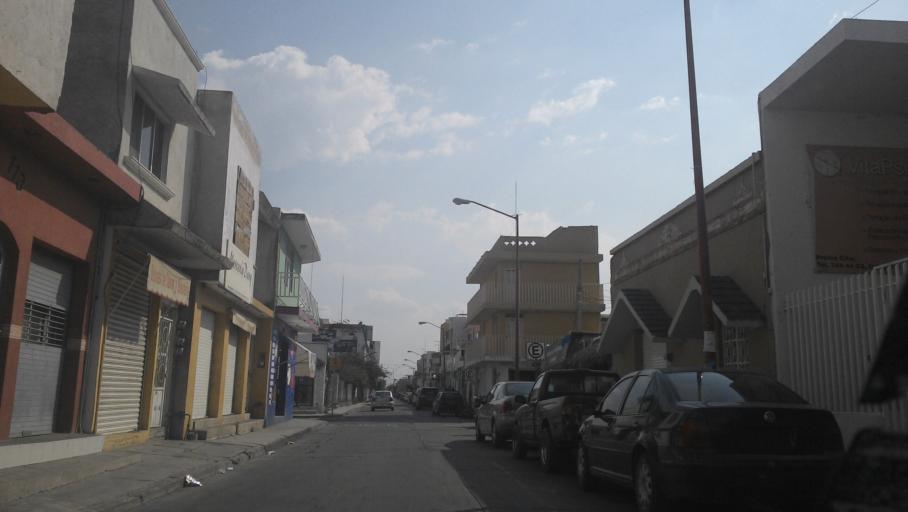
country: MX
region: Guanajuato
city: San Francisco del Rincon
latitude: 21.0175
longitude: -101.8596
